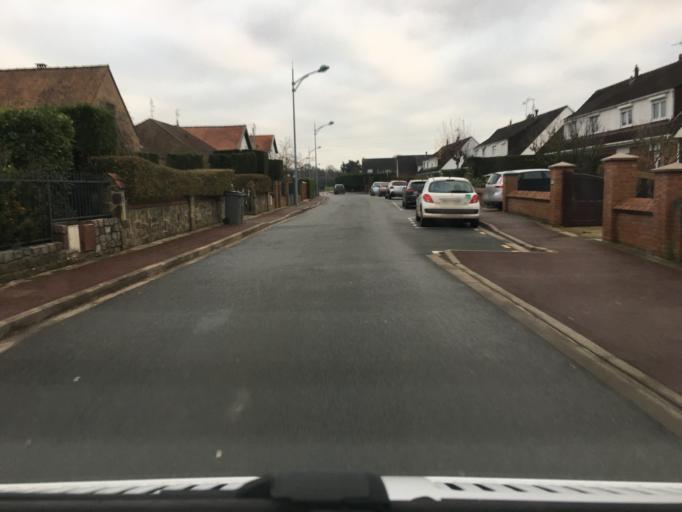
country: FR
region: Nord-Pas-de-Calais
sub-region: Departement du Nord
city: Comines
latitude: 50.7548
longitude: 3.0106
